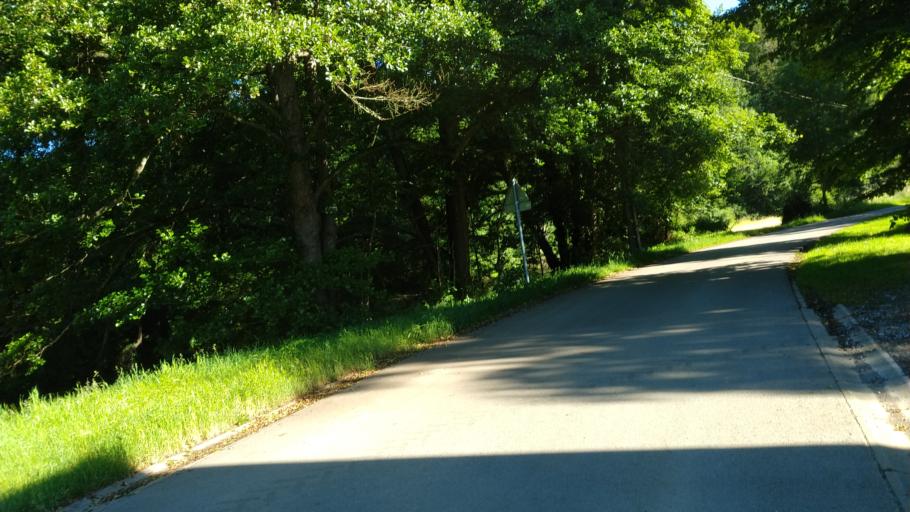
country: BE
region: Wallonia
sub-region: Province du Luxembourg
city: Tellin
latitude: 50.1084
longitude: 5.1971
